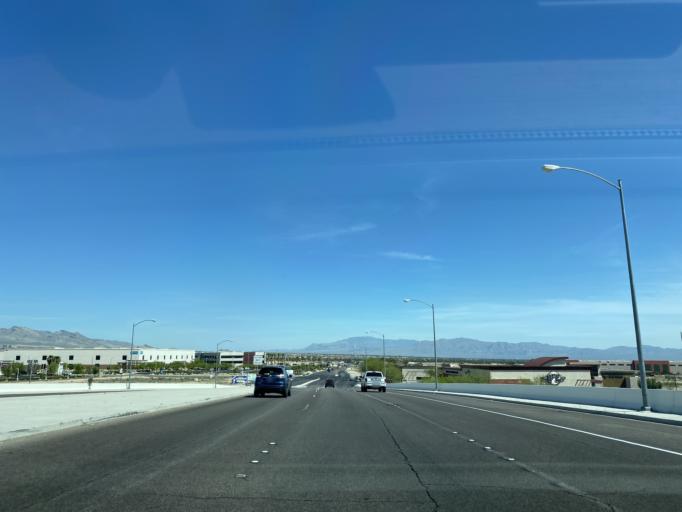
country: US
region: Nevada
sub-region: Clark County
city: Spring Valley
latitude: 36.0681
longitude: -115.2605
